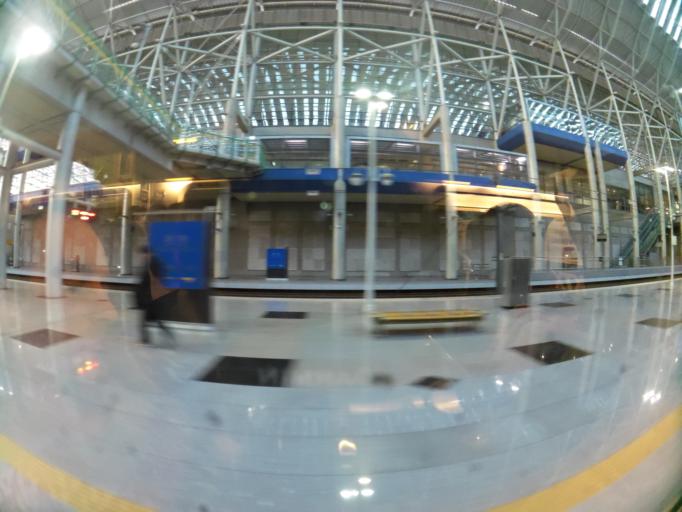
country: KR
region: Gyeonggi-do
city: Anyang-si
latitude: 37.4156
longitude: 126.8839
